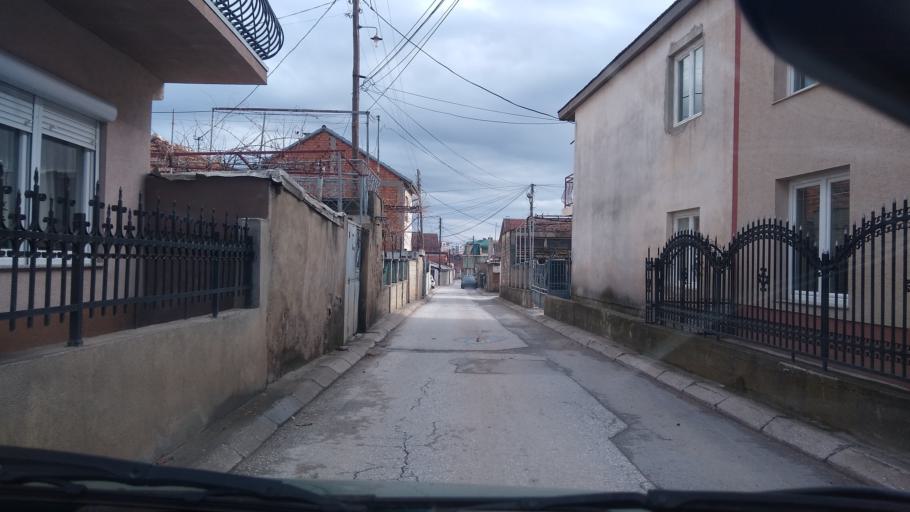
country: MK
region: Bitola
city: Bitola
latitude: 41.0280
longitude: 21.3190
